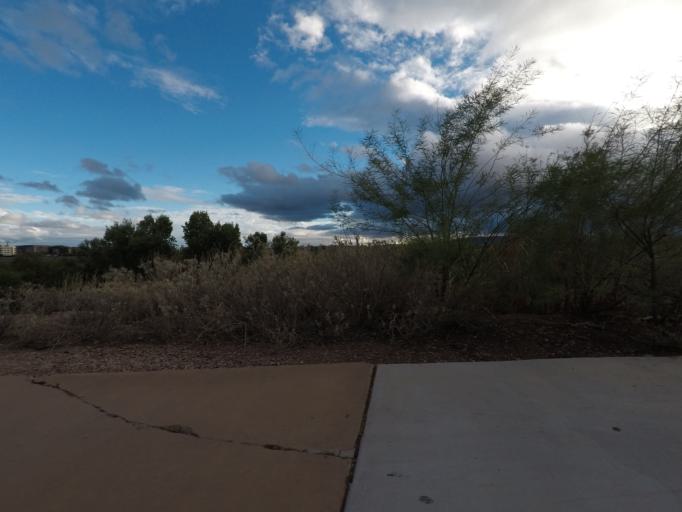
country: US
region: Arizona
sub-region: Maricopa County
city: Tempe Junction
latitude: 33.4357
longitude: -111.9538
